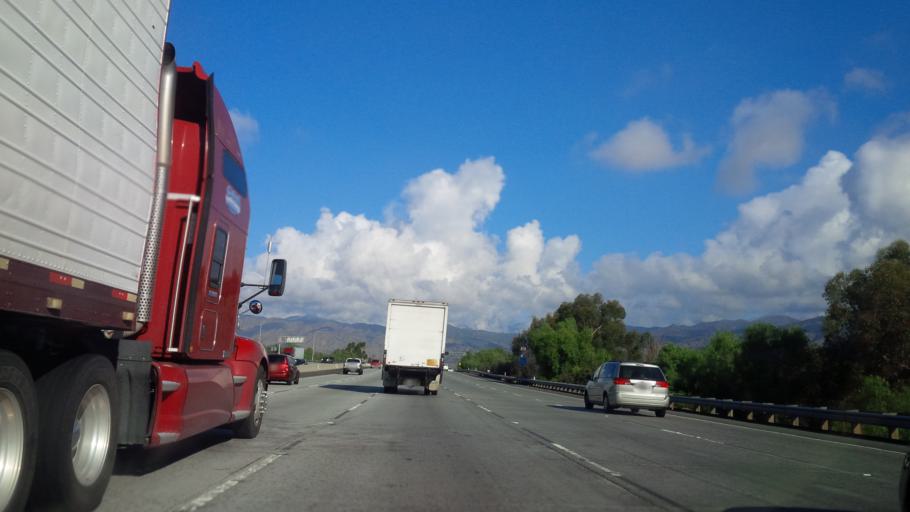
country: US
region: California
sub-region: Los Angeles County
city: San Dimas
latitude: 34.1082
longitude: -117.8223
